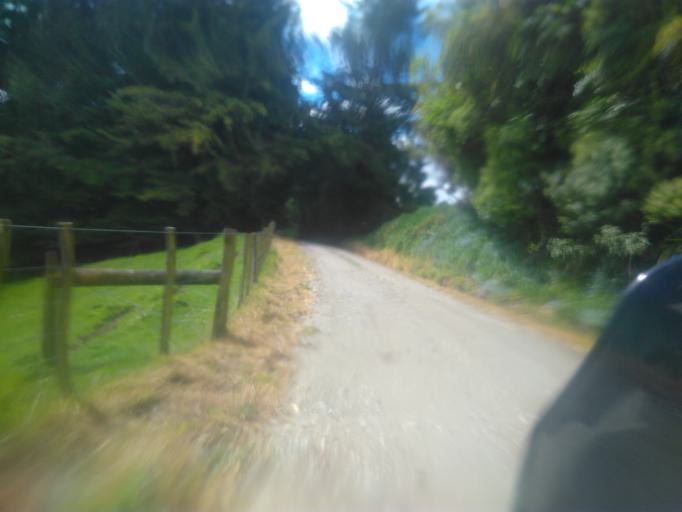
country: NZ
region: Hawke's Bay
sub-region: Wairoa District
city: Wairoa
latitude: -38.7742
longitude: 177.6374
